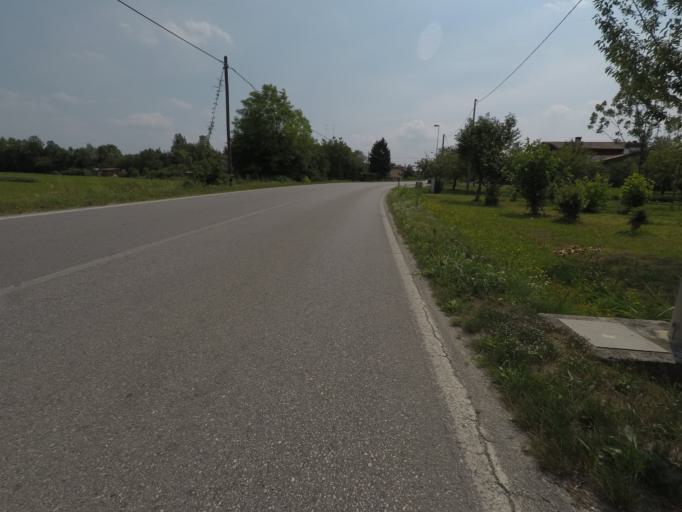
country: IT
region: Friuli Venezia Giulia
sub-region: Provincia di Pordenone
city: Caneva
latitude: 45.9886
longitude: 12.4783
